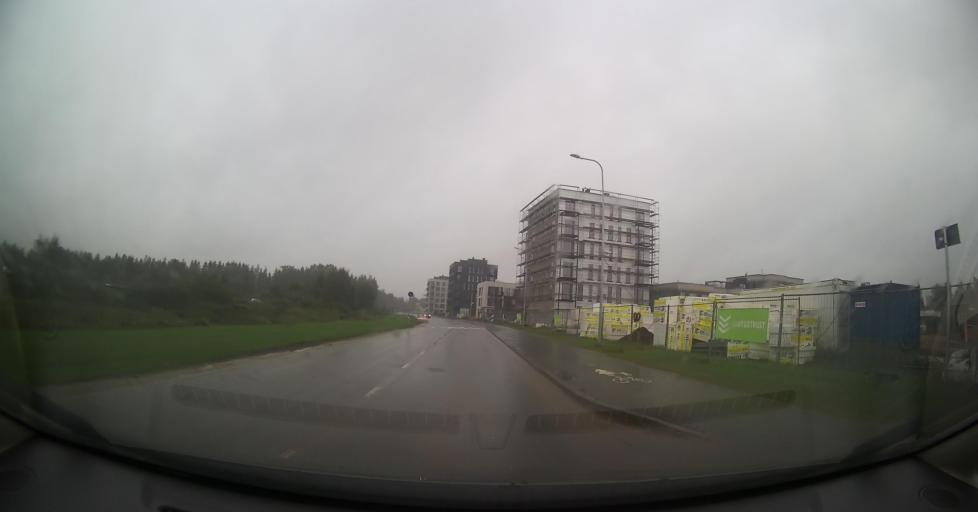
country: EE
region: Tartu
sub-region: Tartu linn
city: Tartu
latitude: 58.3655
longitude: 26.7654
